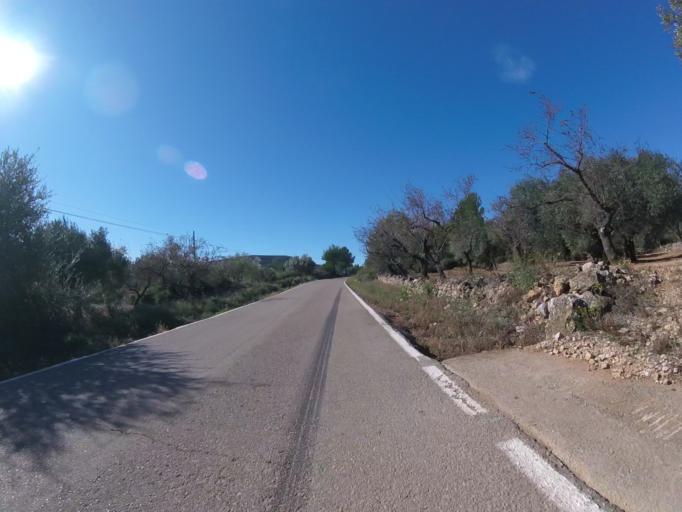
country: ES
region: Valencia
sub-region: Provincia de Castello
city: Chert/Xert
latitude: 40.4482
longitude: 0.1113
